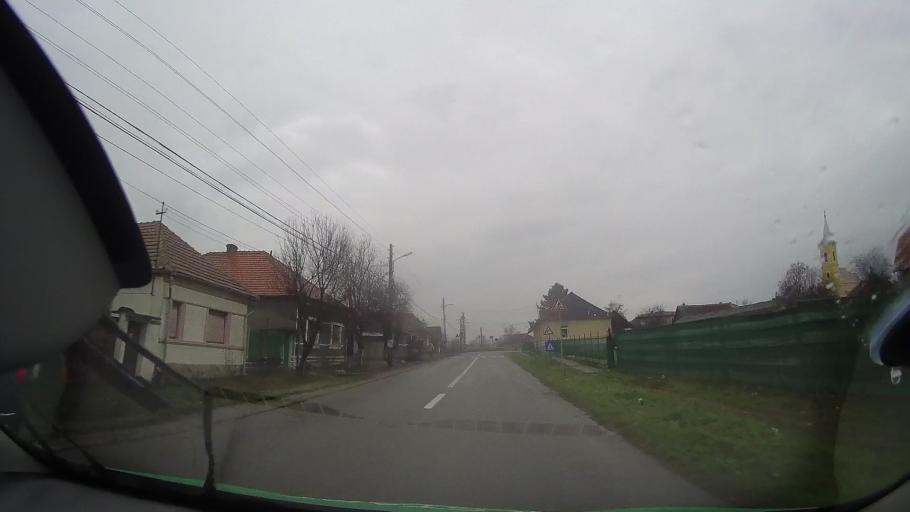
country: RO
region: Bihor
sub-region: Comuna Tinca
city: Tinca
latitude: 46.7396
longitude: 21.9456
